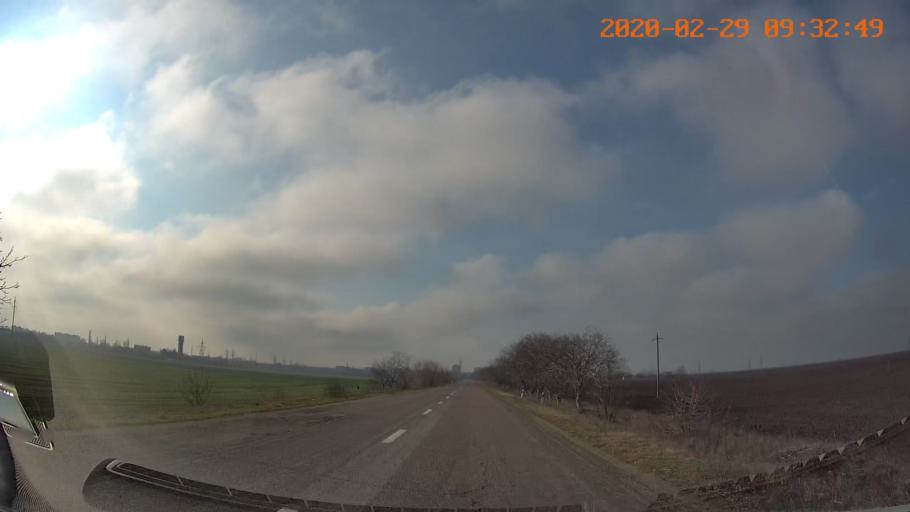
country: MD
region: Telenesti
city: Dnestrovsc
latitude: 46.6345
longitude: 29.9041
